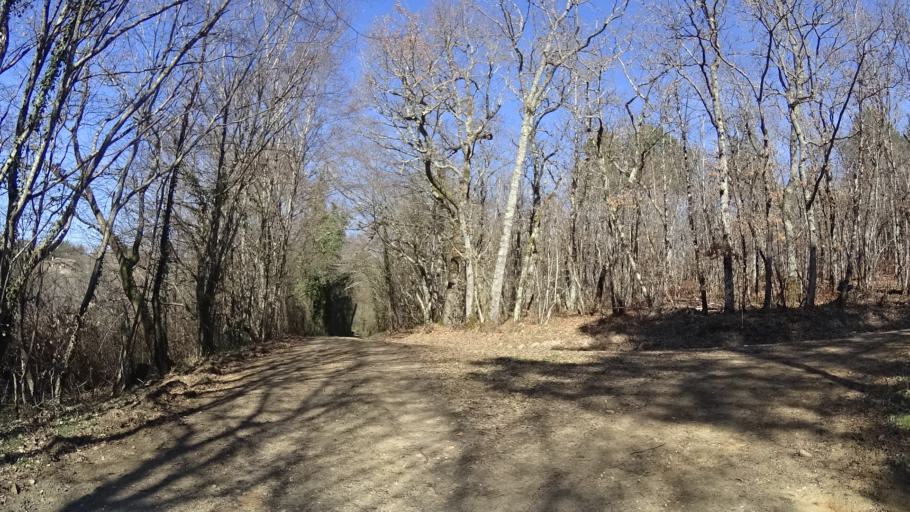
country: FR
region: Aquitaine
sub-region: Departement de la Dordogne
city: Riberac
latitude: 45.1972
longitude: 0.3142
